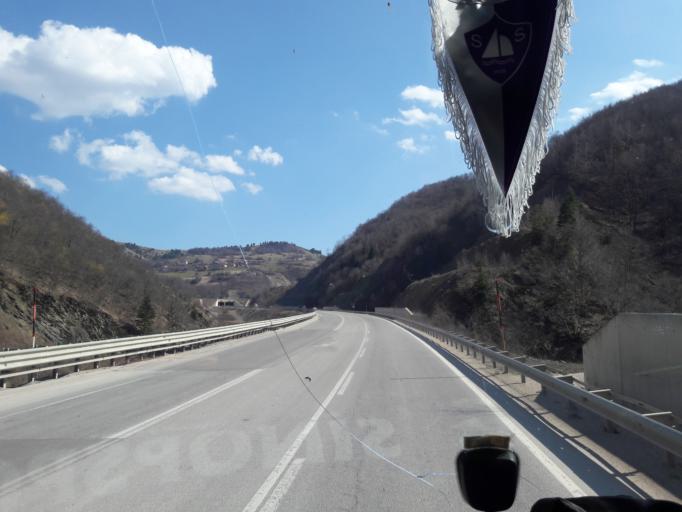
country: TR
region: Sinop
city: Erfelek
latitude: 41.6792
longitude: 34.9099
